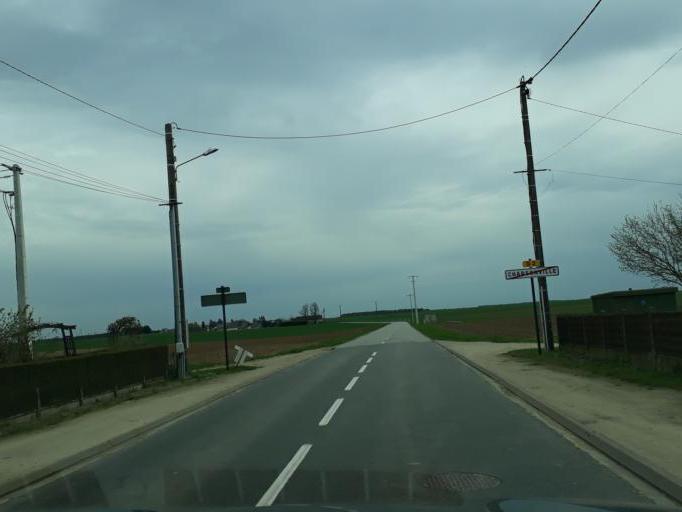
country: FR
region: Centre
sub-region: Departement du Loiret
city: Epieds-en-Beauce
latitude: 47.9256
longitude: 1.5836
